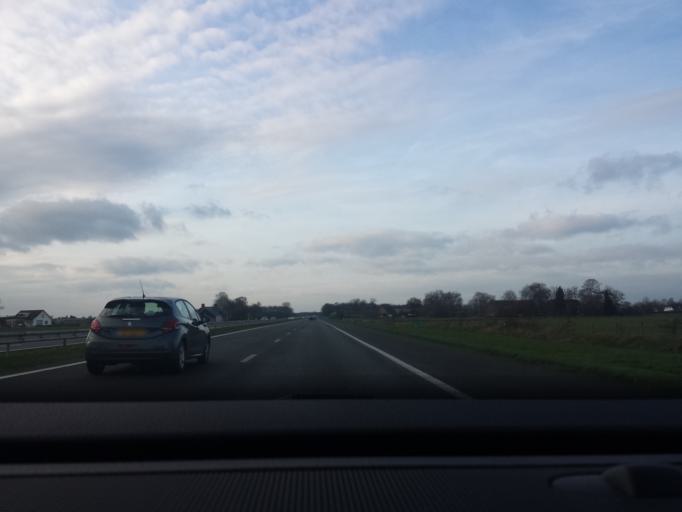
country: NL
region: Gelderland
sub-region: Gemeente Doetinchem
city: Doetinchem
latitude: 51.9436
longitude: 6.2531
